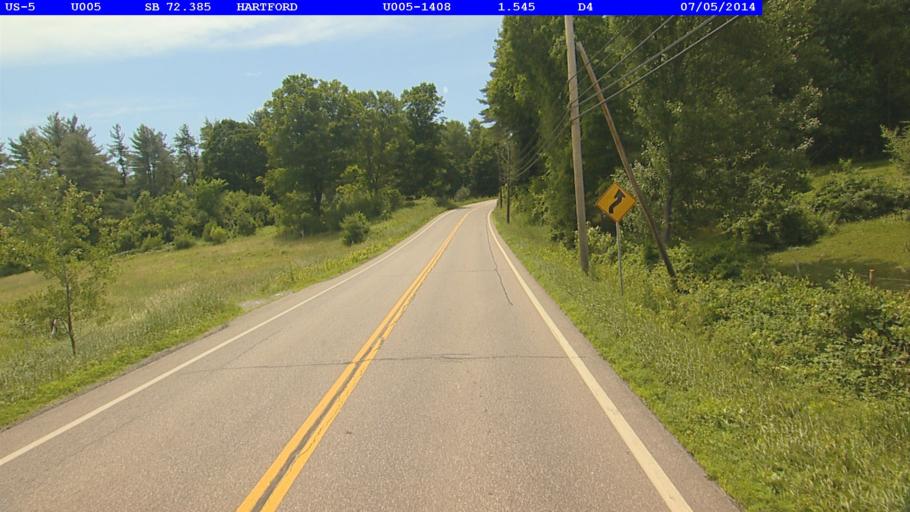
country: US
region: Vermont
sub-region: Windsor County
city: White River Junction
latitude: 43.6322
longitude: -72.3495
